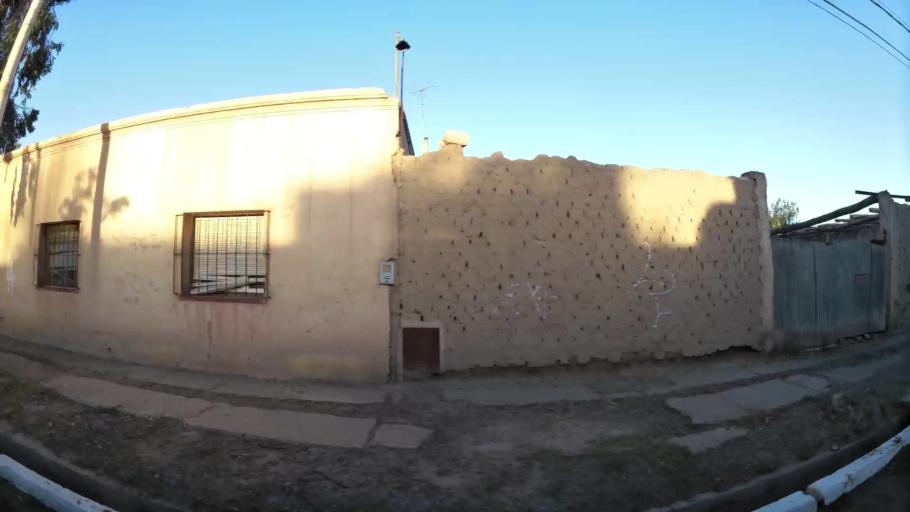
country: AR
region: San Juan
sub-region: Departamento de Santa Lucia
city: Santa Lucia
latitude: -31.5234
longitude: -68.5075
